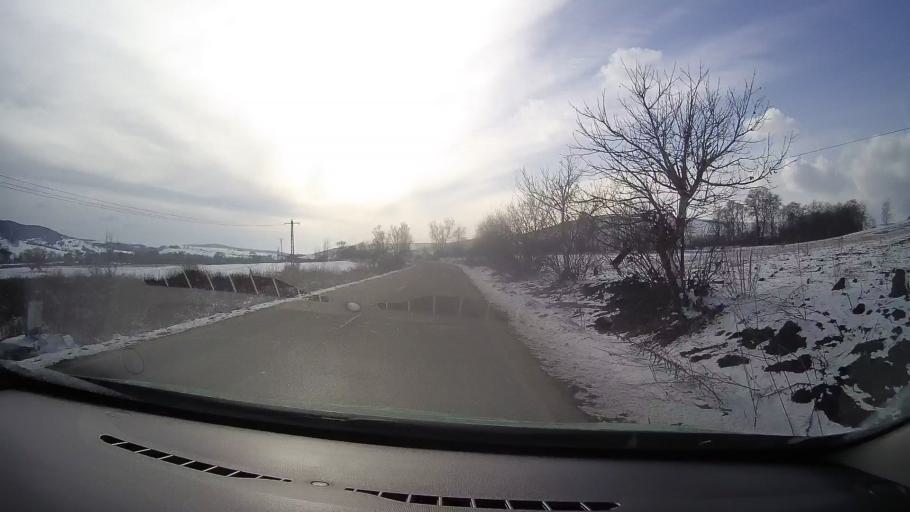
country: RO
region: Sibiu
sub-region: Comuna Iacobeni
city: Iacobeni
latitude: 46.0313
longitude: 24.7158
